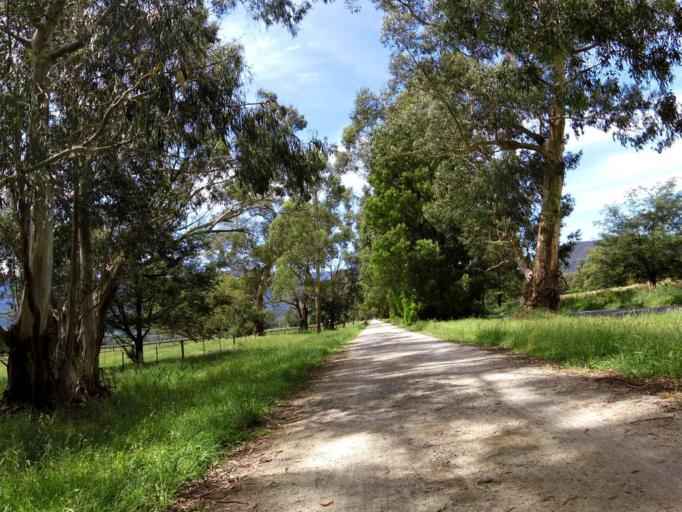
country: AU
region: Victoria
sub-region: Yarra Ranges
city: Yarra Junction
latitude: -37.7750
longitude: 145.6246
